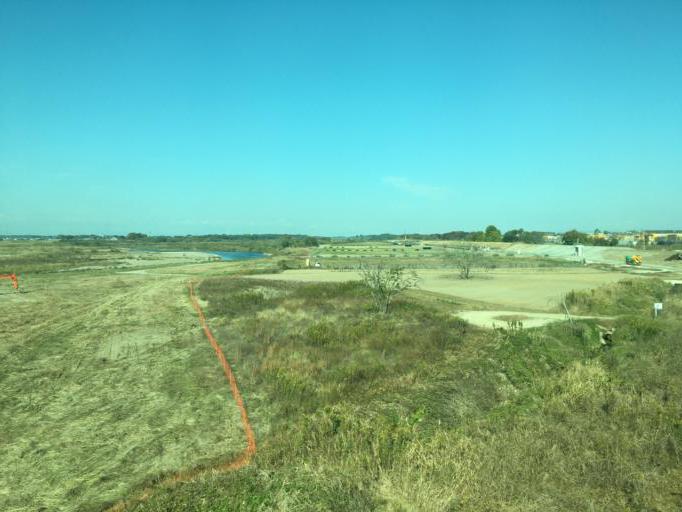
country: JP
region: Ibaraki
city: Yuki
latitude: 36.2962
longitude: 139.9108
